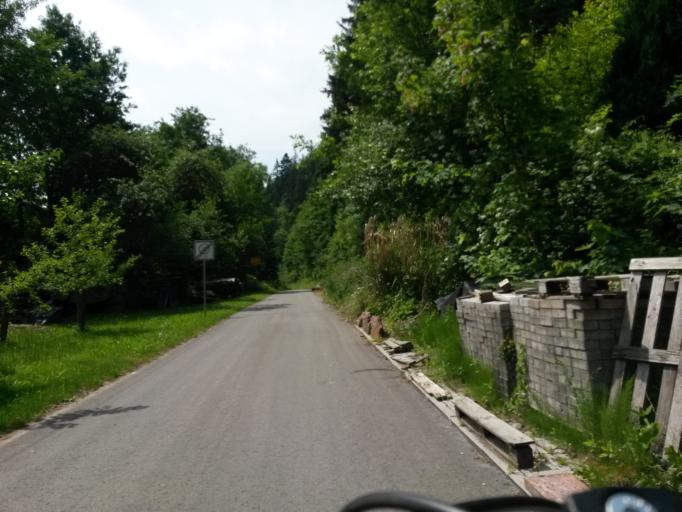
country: DE
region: Baden-Wuerttemberg
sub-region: Karlsruhe Region
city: Neubulach
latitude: 48.6641
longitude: 8.7250
